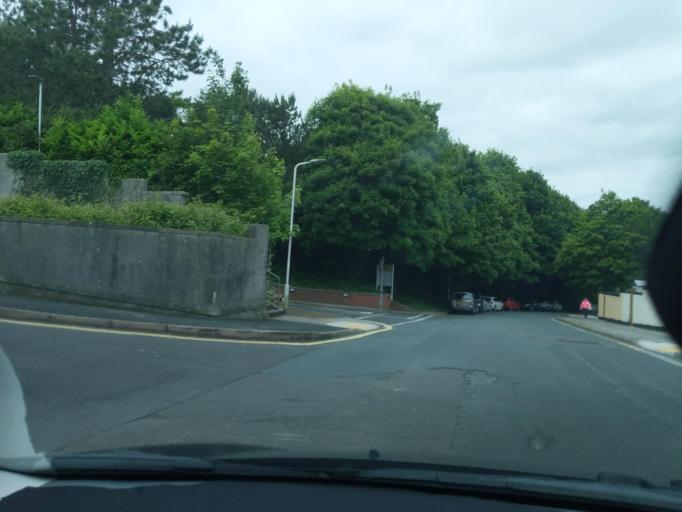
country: GB
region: England
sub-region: Plymouth
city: Plymouth
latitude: 50.4074
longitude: -4.1269
